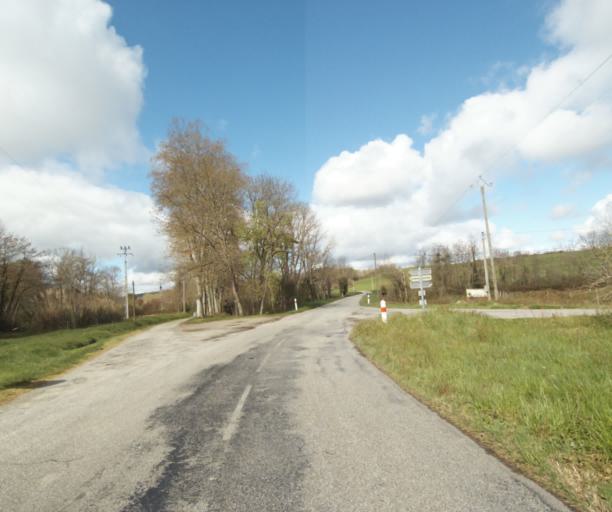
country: FR
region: Midi-Pyrenees
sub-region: Departement de l'Ariege
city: Saverdun
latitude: 43.2264
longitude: 1.5582
